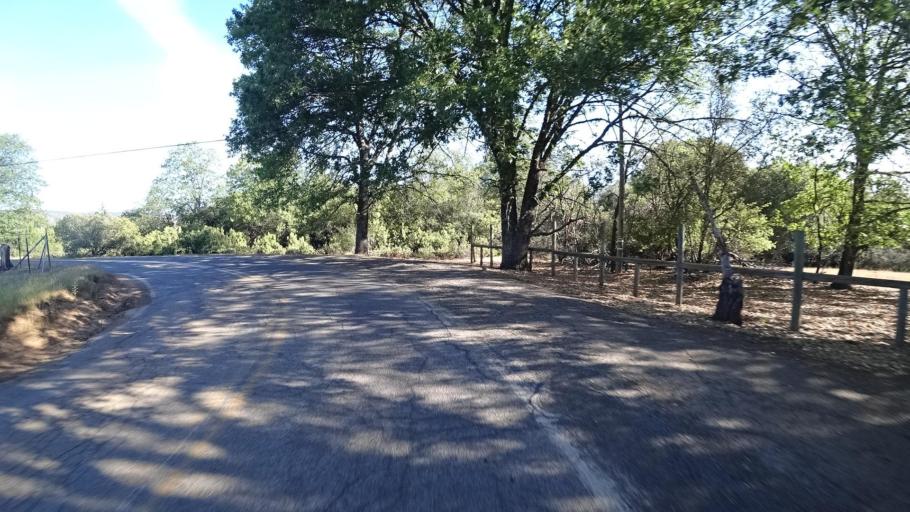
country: US
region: California
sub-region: Lake County
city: Lakeport
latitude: 39.0440
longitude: -122.9509
